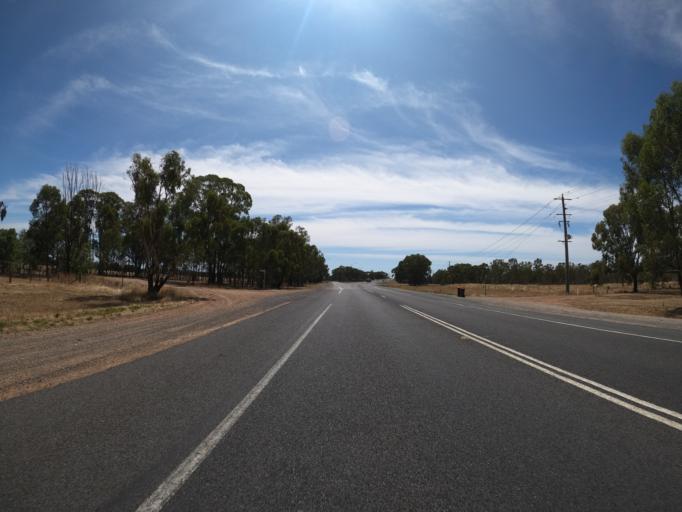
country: AU
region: Victoria
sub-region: Benalla
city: Benalla
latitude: -36.5234
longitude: 146.0570
